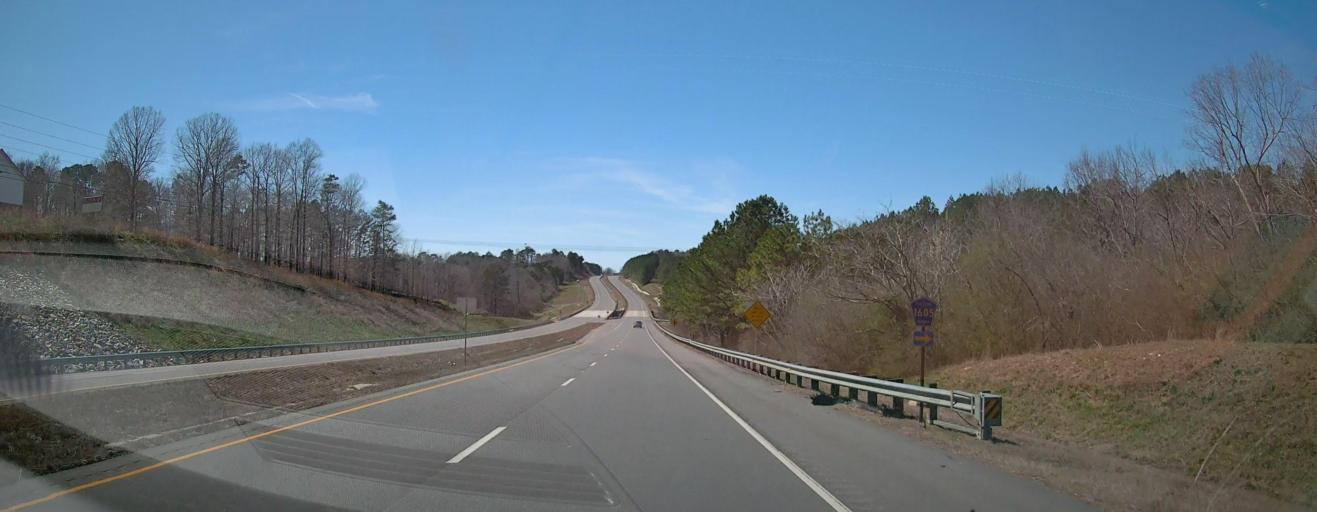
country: US
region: Alabama
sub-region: Cullman County
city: Cullman
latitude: 34.1823
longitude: -86.7696
